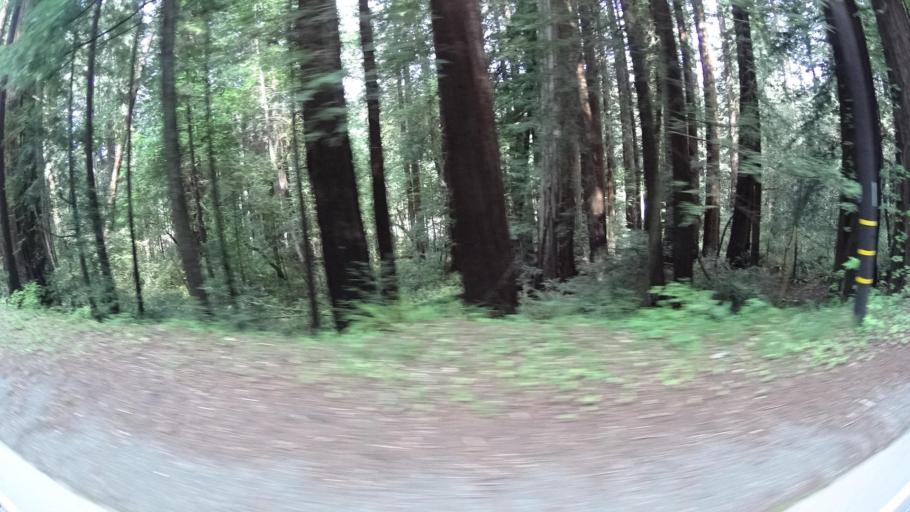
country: US
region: California
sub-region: Humboldt County
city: Redway
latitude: 40.1318
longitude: -123.8176
